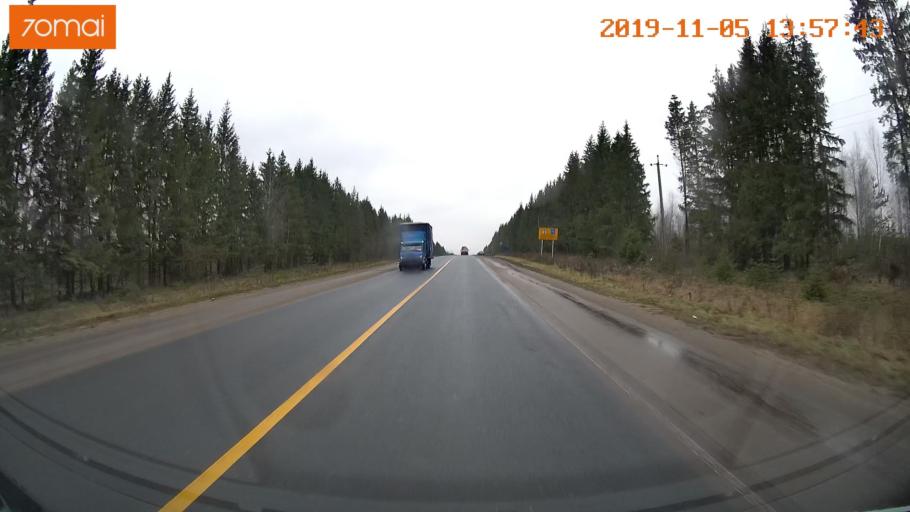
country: RU
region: Ivanovo
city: Kitovo
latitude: 57.0294
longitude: 41.3029
